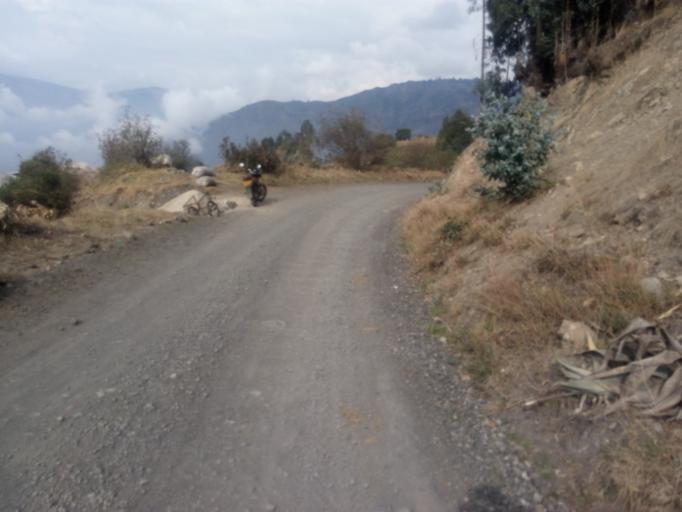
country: CO
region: Boyaca
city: Chita
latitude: 6.1924
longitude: -72.4779
